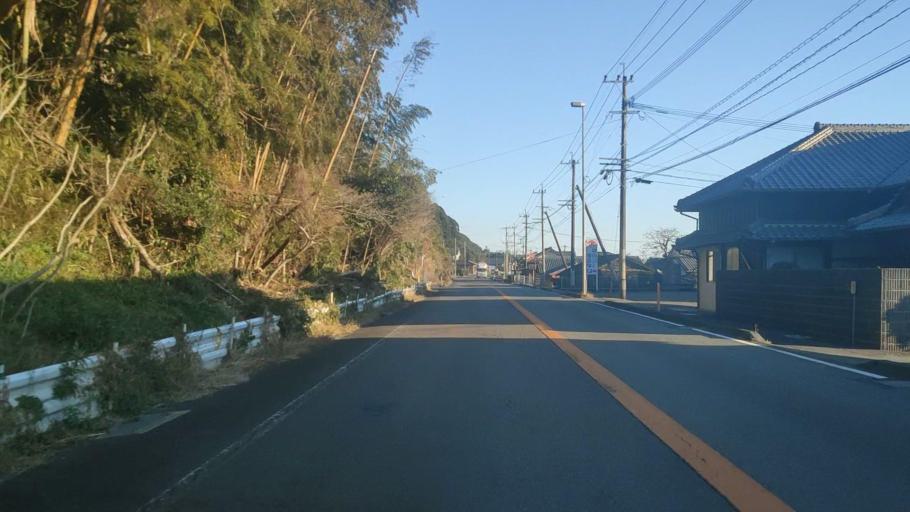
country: JP
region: Miyazaki
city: Takanabe
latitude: 32.0824
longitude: 131.5099
